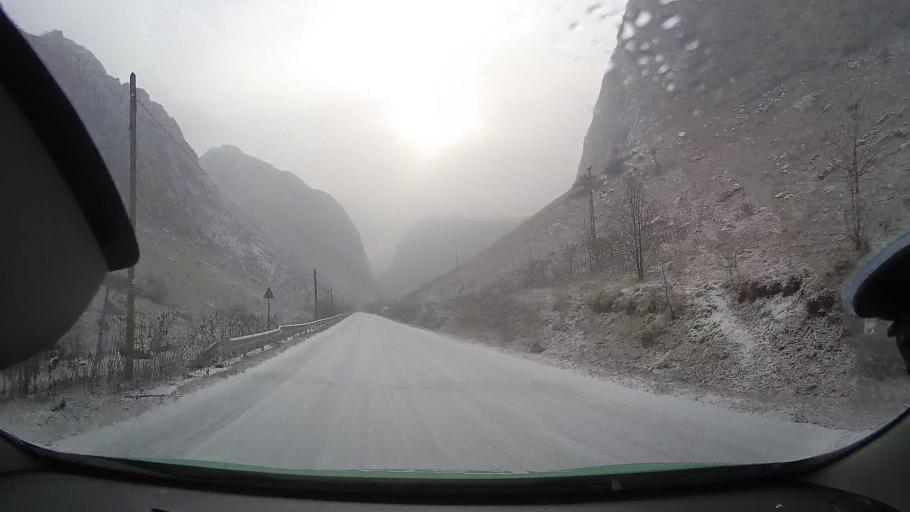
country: RO
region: Alba
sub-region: Comuna Livezile
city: Livezile
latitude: 46.3822
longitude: 23.5811
